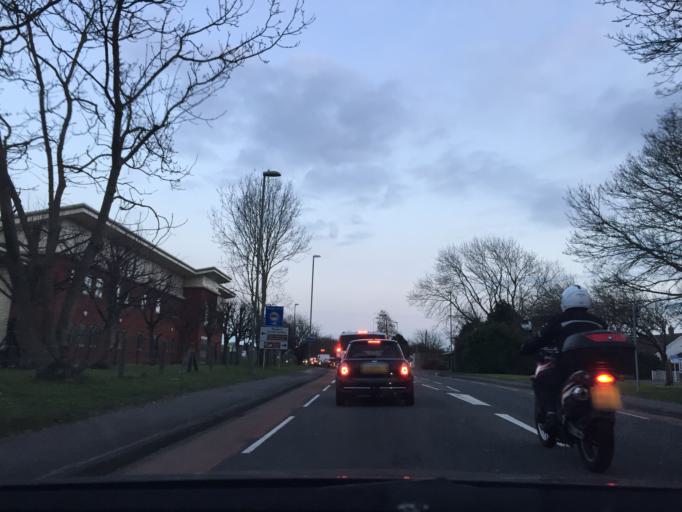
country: GB
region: England
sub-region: Hampshire
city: Fareham
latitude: 50.8226
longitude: -1.1643
